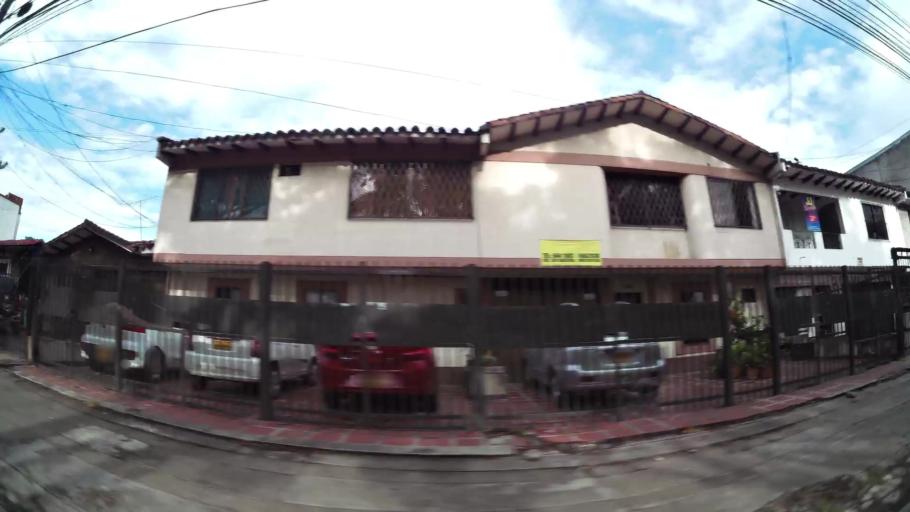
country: CO
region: Valle del Cauca
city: Cali
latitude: 3.4869
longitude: -76.5200
